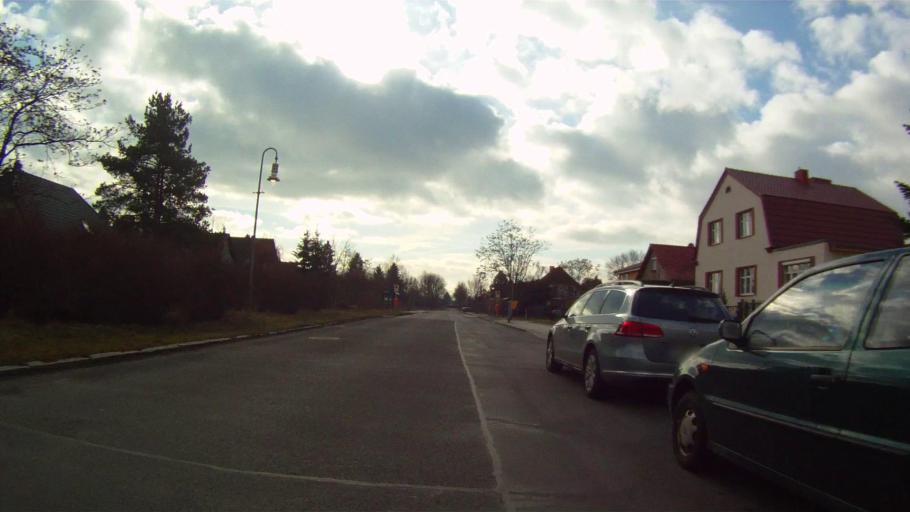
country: DE
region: Berlin
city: Biesdorf
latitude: 52.4953
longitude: 13.5552
